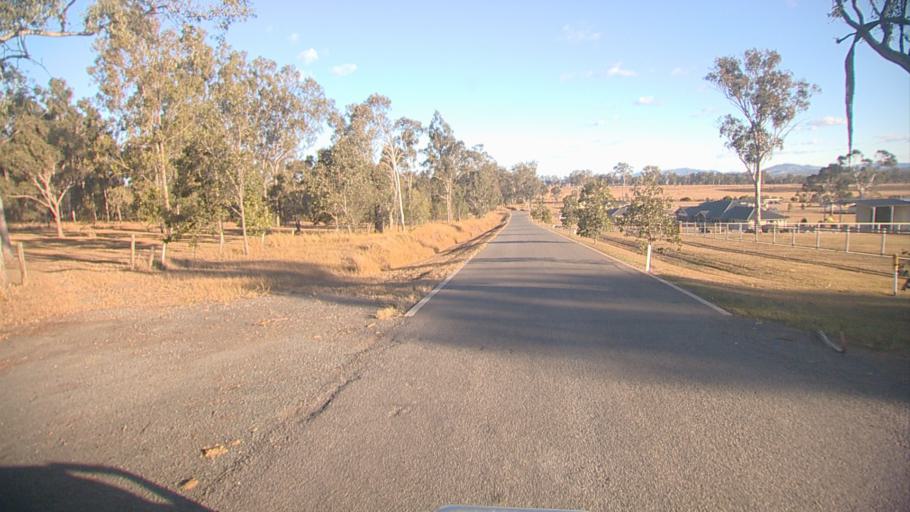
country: AU
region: Queensland
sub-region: Logan
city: Cedar Vale
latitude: -27.8725
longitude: 152.9747
